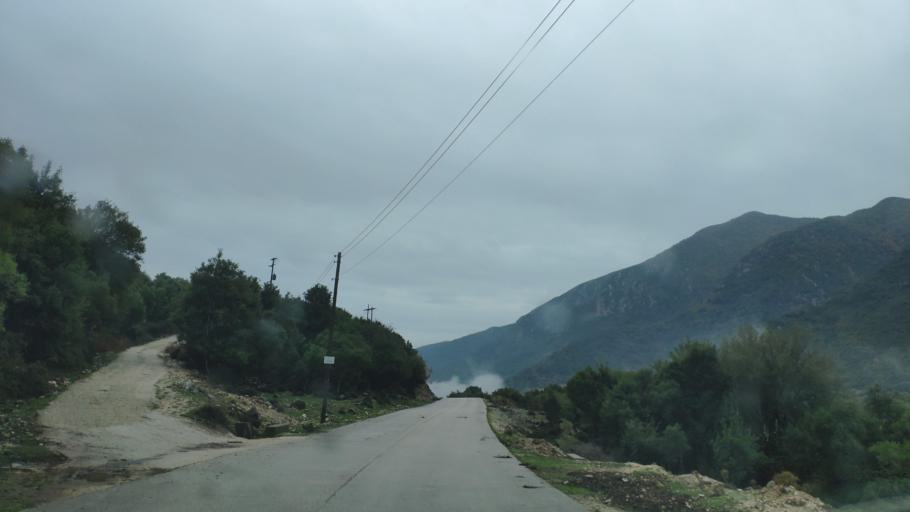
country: GR
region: Epirus
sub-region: Nomos Thesprotias
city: Paramythia
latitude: 39.3941
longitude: 20.6241
